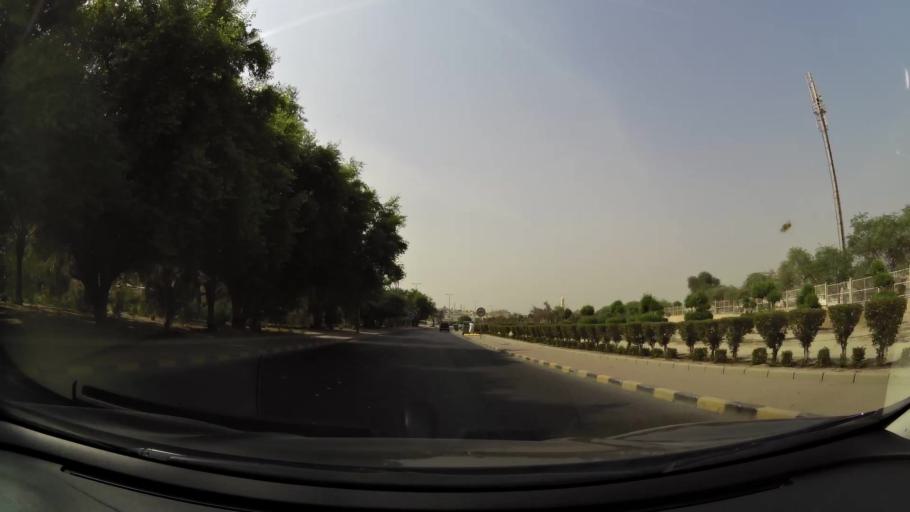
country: KW
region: Al Asimah
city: Ar Rabiyah
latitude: 29.3032
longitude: 47.8878
